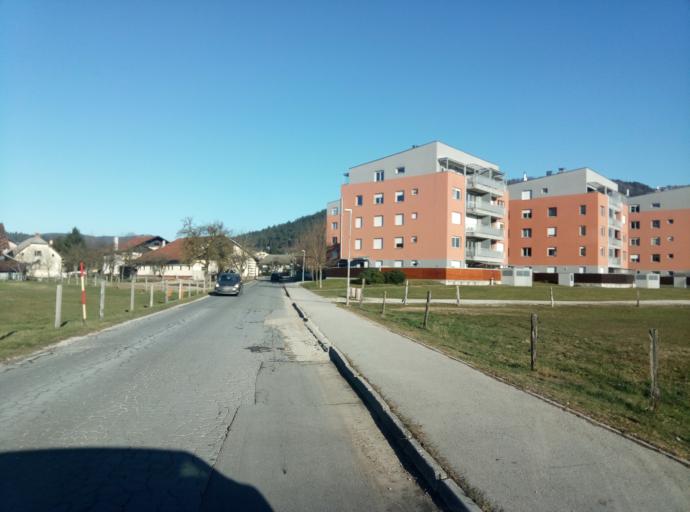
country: SI
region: Cerknica
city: Cerknica
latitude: 45.7907
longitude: 14.3617
